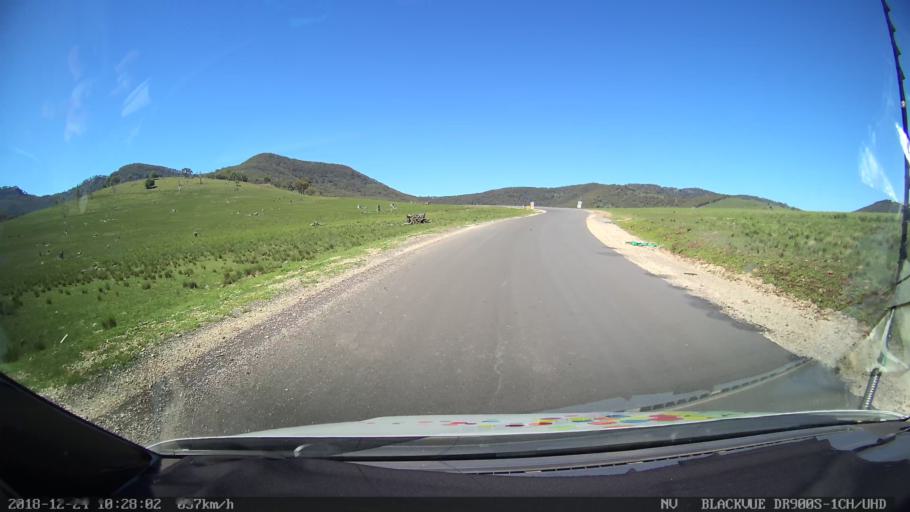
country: AU
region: New South Wales
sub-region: Liverpool Plains
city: Quirindi
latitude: -31.8246
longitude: 150.5314
